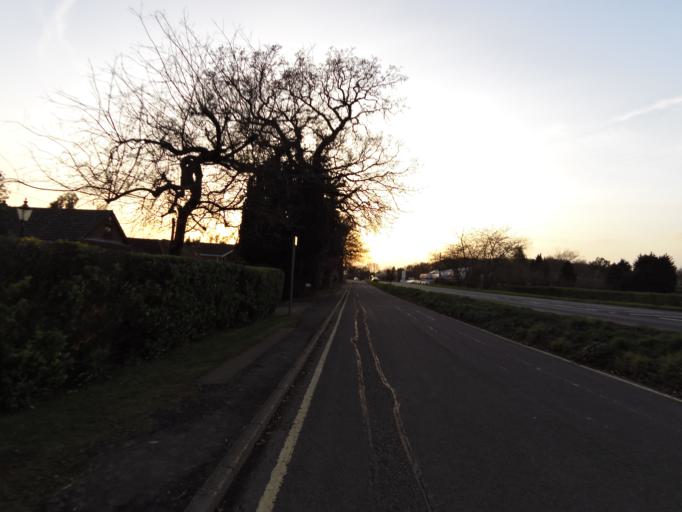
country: GB
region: England
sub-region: Suffolk
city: Kesgrave
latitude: 52.0272
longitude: 1.2342
